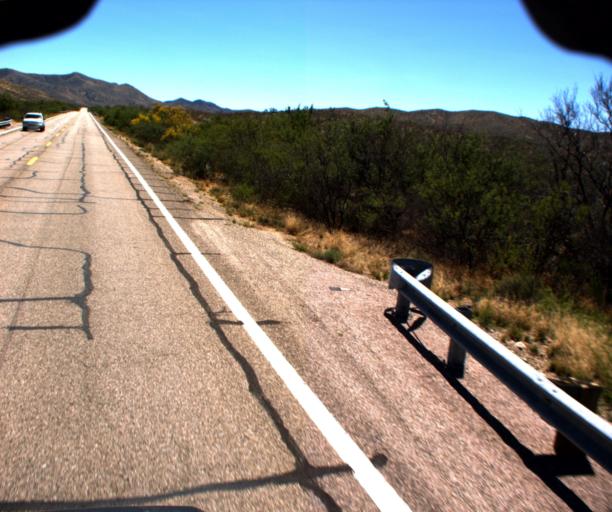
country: US
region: Arizona
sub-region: Pima County
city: Corona de Tucson
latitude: 31.9419
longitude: -110.6633
